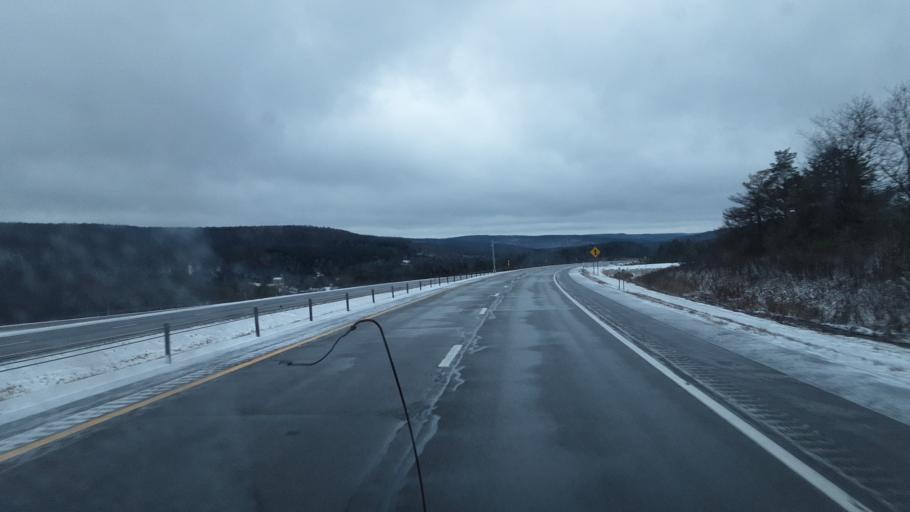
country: US
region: New York
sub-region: Allegany County
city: Alfred
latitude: 42.3066
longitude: -77.8731
